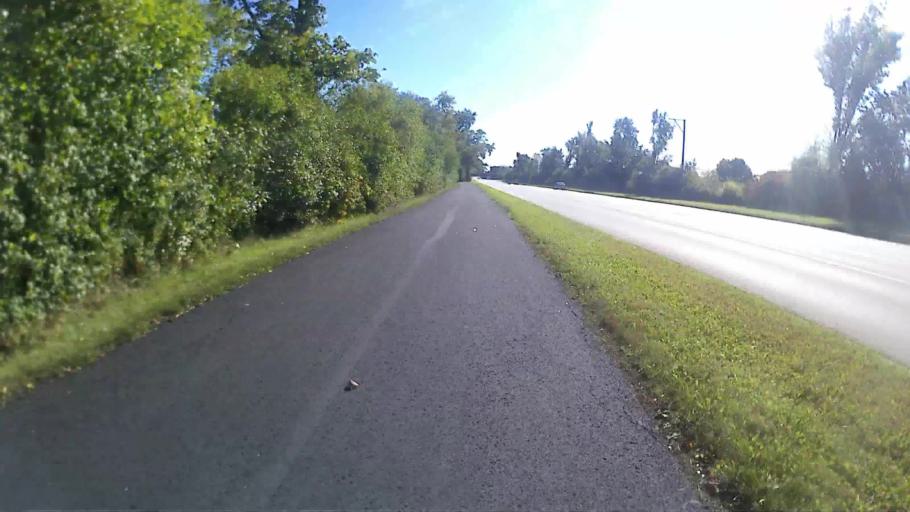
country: US
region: Illinois
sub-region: DuPage County
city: Addison
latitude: 41.9473
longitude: -87.9885
